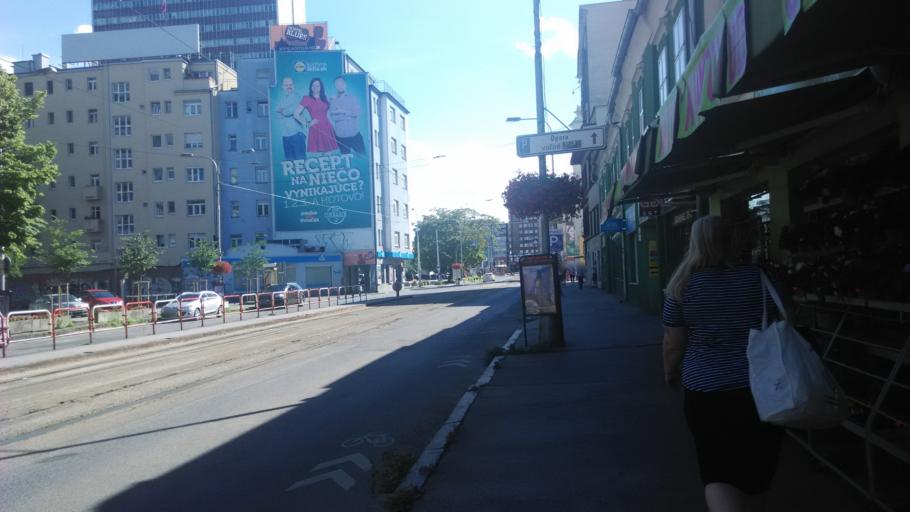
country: SK
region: Bratislavsky
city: Bratislava
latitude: 48.1474
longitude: 17.1155
